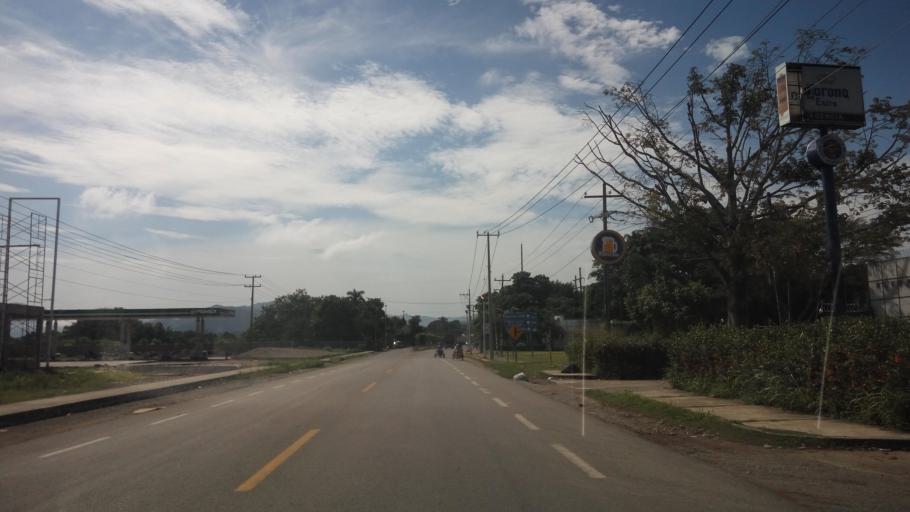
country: MX
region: Tabasco
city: Teapa
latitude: 17.5717
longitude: -92.9567
